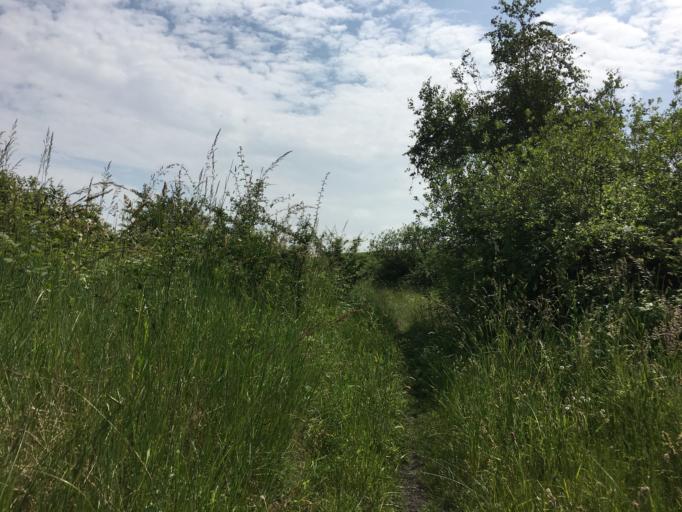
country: GB
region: England
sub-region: Kent
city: Sittingbourne
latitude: 51.3657
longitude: 0.7632
